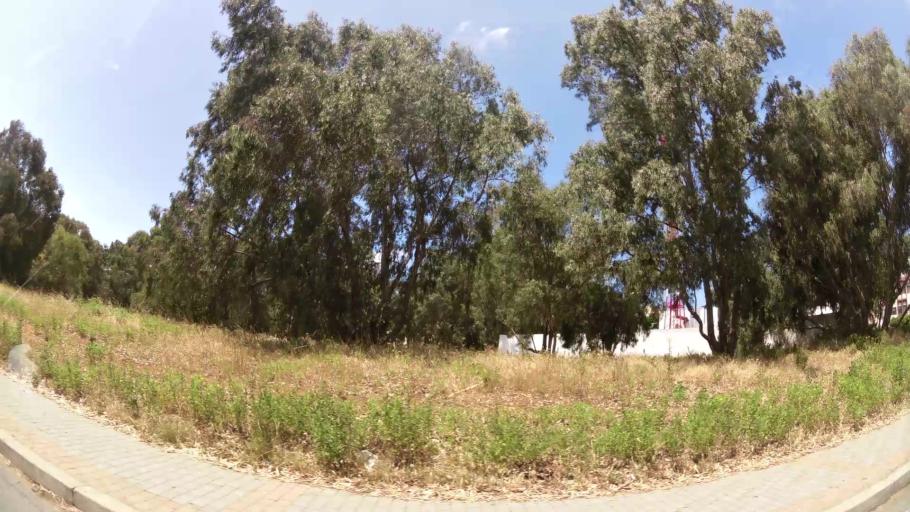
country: MA
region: Gharb-Chrarda-Beni Hssen
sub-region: Kenitra Province
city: Kenitra
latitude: 34.2632
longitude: -6.6130
